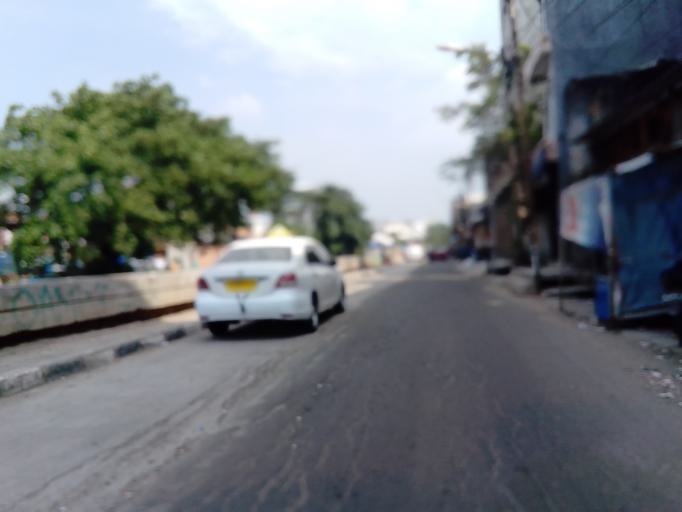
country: ID
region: Jakarta Raya
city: Jakarta
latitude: -6.1487
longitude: 106.8118
